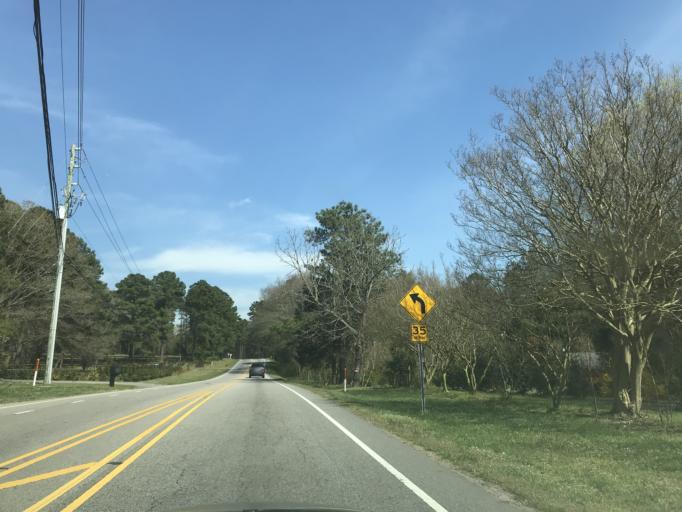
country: US
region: North Carolina
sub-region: Wake County
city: Knightdale
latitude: 35.8343
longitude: -78.5481
